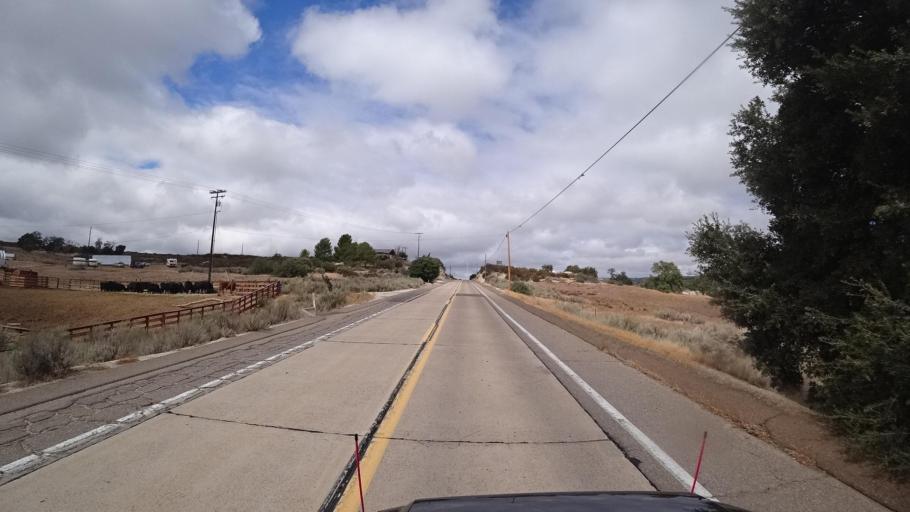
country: US
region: California
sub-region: San Diego County
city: Campo
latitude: 32.6900
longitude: -116.3393
